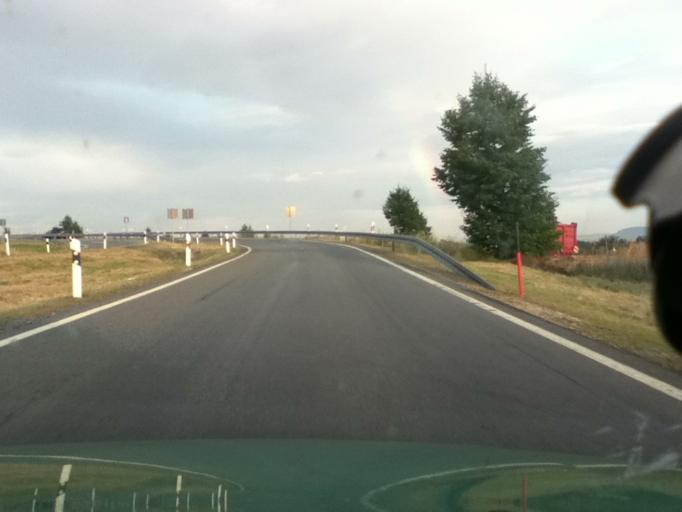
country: DE
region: Saxony
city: Weissenberg
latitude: 51.2059
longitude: 14.6620
